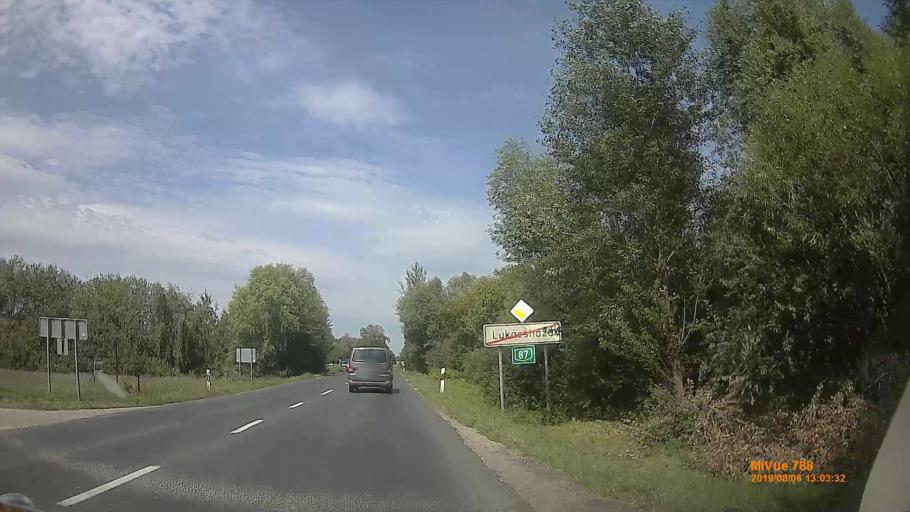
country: HU
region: Vas
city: Koszeg
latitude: 47.3432
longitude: 16.5773
